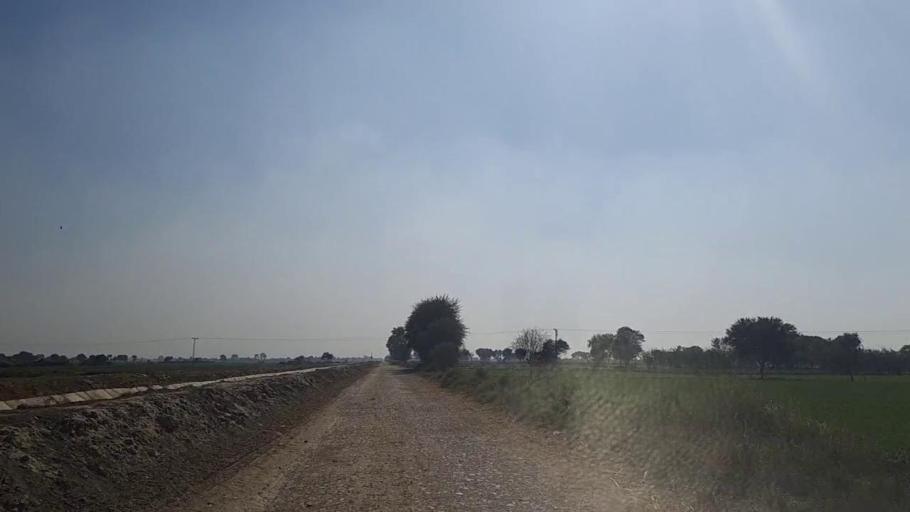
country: PK
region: Sindh
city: Shahpur Chakar
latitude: 26.2065
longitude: 68.5838
